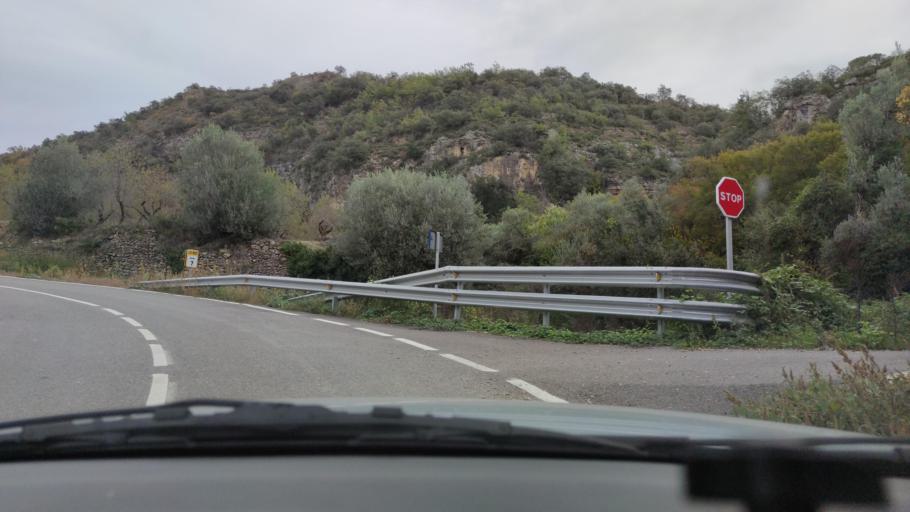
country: ES
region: Catalonia
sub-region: Provincia de Lleida
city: Llimiana
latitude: 42.0724
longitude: 0.9176
